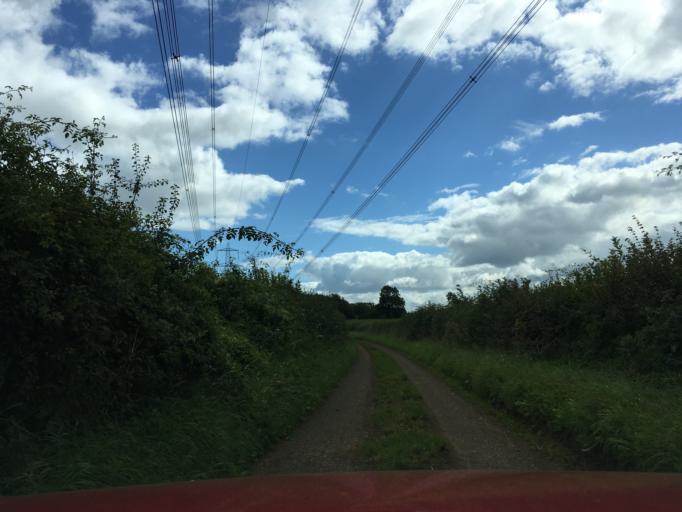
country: GB
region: England
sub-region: Wiltshire
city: Nettleton
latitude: 51.5082
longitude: -2.2264
